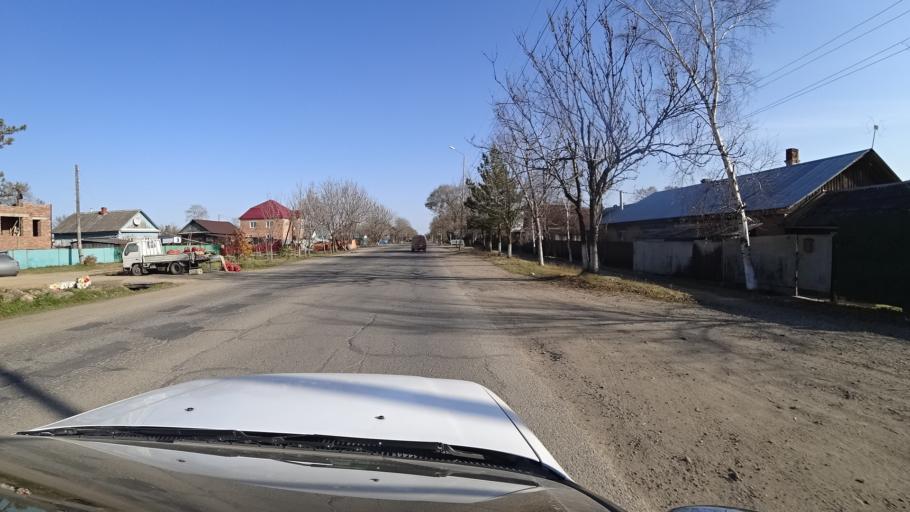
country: RU
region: Primorskiy
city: Dal'nerechensk
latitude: 45.9226
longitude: 133.7479
